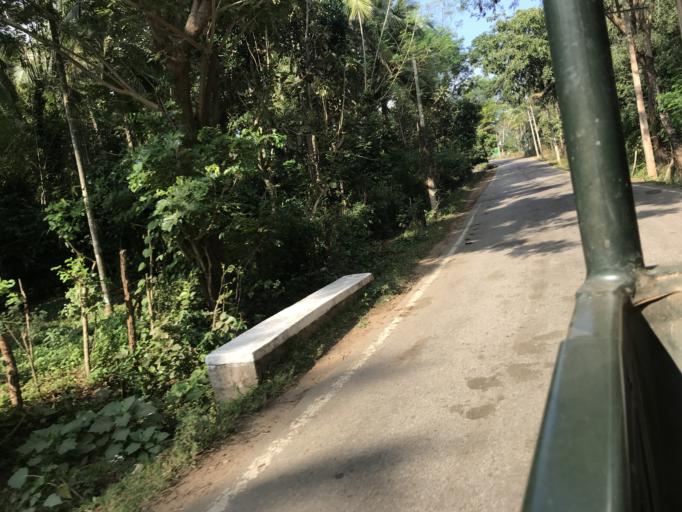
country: IN
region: Karnataka
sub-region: Mysore
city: Heggadadevankote
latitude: 11.9452
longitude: 76.2427
